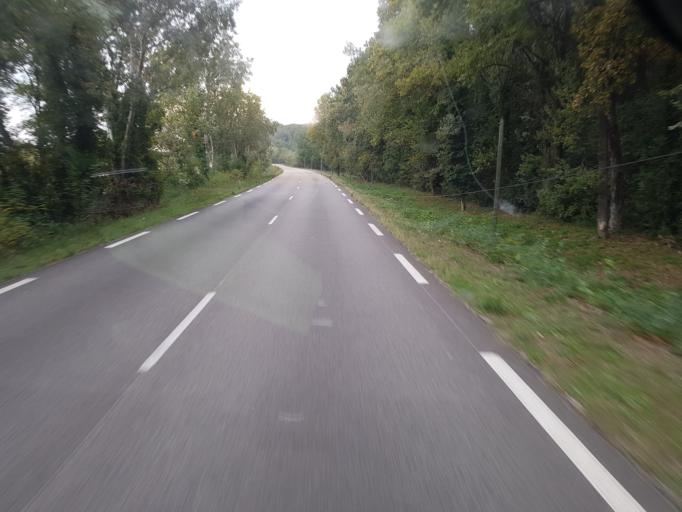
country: FR
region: Languedoc-Roussillon
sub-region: Departement du Gard
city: Les Angles
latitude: 43.9359
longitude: 4.7502
